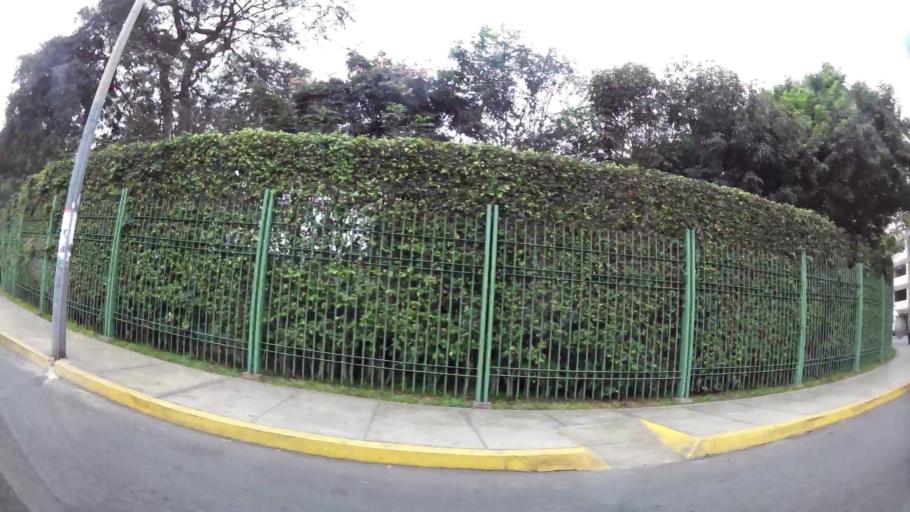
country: PE
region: Lima
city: Lima
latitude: -12.0730
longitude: -77.0336
